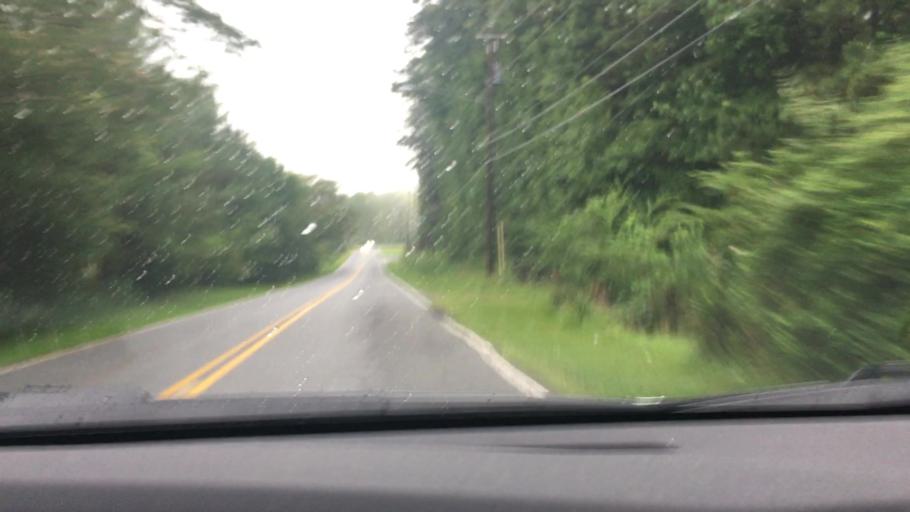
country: US
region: Georgia
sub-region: Fulton County
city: Union City
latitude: 33.6394
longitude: -84.5248
